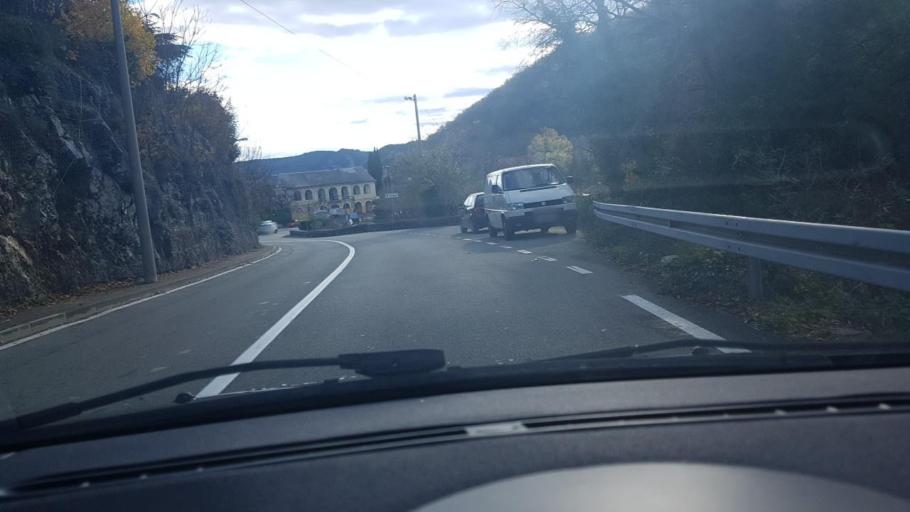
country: HR
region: Primorsko-Goranska
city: Cavle
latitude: 45.3380
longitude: 14.4670
